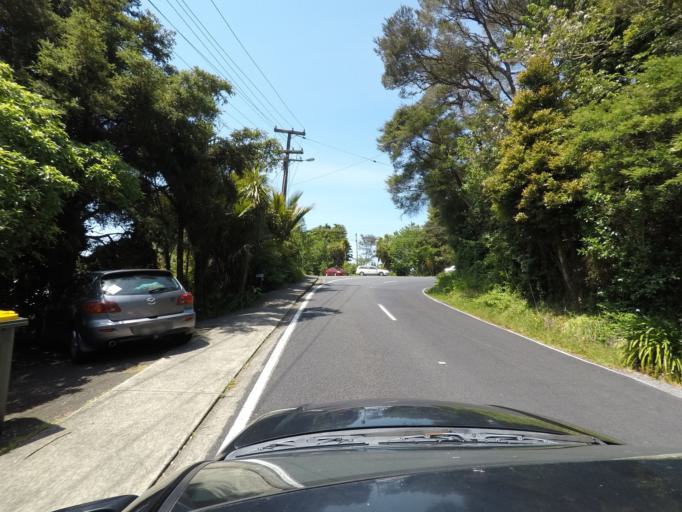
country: NZ
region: Auckland
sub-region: Auckland
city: Titirangi
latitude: -36.9619
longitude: 174.6406
